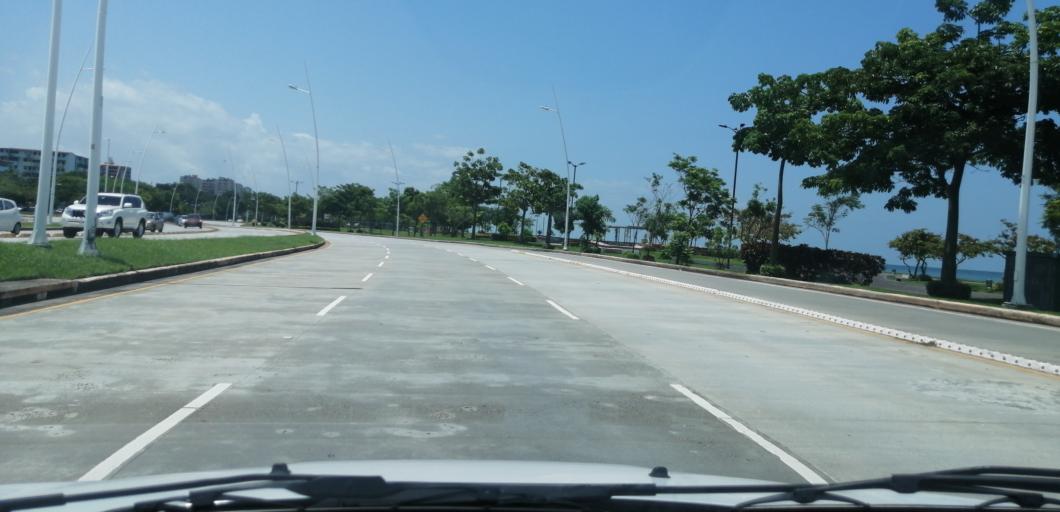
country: PA
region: Panama
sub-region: Distrito de Panama
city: Ancon
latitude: 8.9467
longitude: -79.5480
